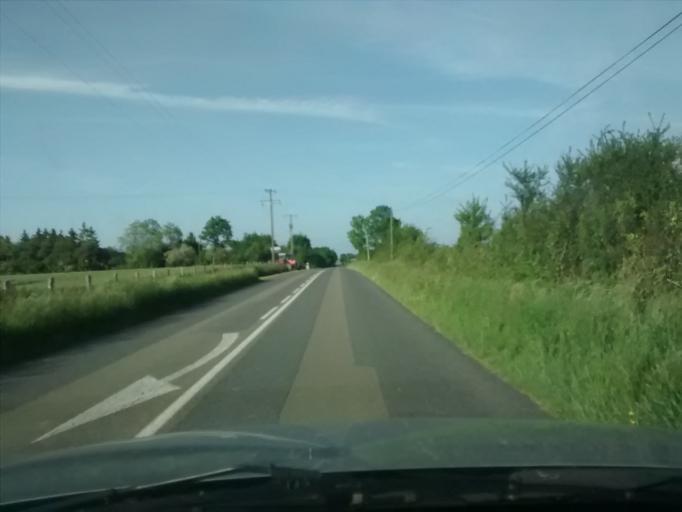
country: FR
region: Pays de la Loire
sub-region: Departement de la Mayenne
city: Meslay-du-Maine
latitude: 47.9915
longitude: -0.6069
